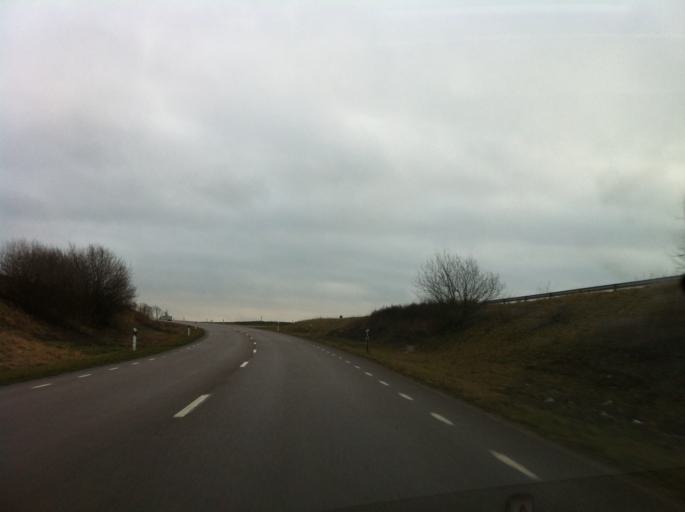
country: SE
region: Skane
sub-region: Helsingborg
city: Glumslov
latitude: 55.9569
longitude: 12.7943
